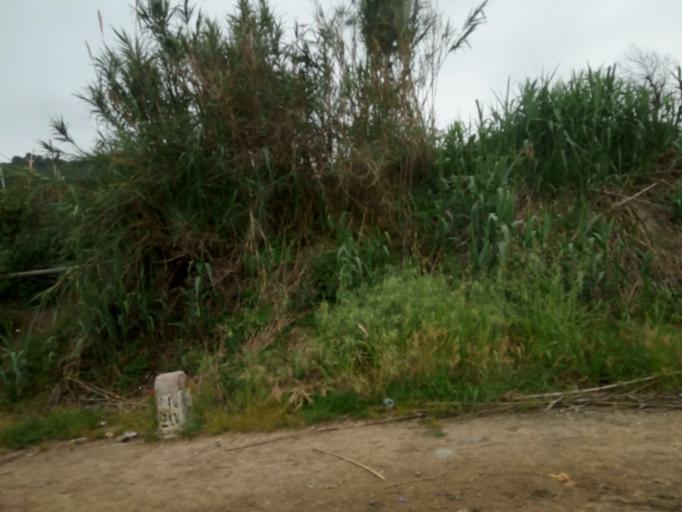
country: DZ
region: Tipaza
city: Tipasa
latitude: 36.5898
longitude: 2.5455
